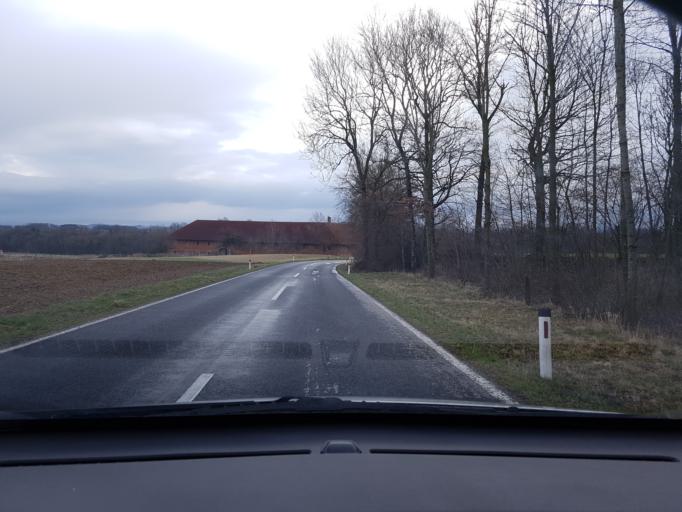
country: AT
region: Upper Austria
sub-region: Politischer Bezirk Linz-Land
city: Sankt Florian
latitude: 48.1510
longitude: 14.3686
